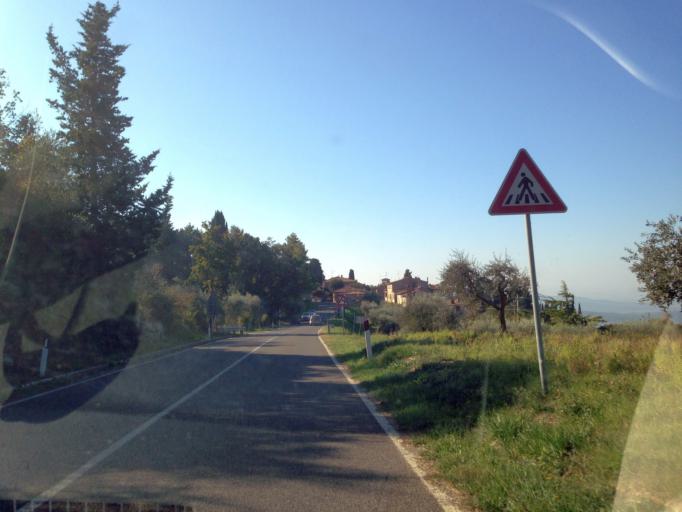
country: IT
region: Tuscany
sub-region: Provincia di Siena
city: Castellina in Chianti
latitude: 43.4376
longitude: 11.3078
